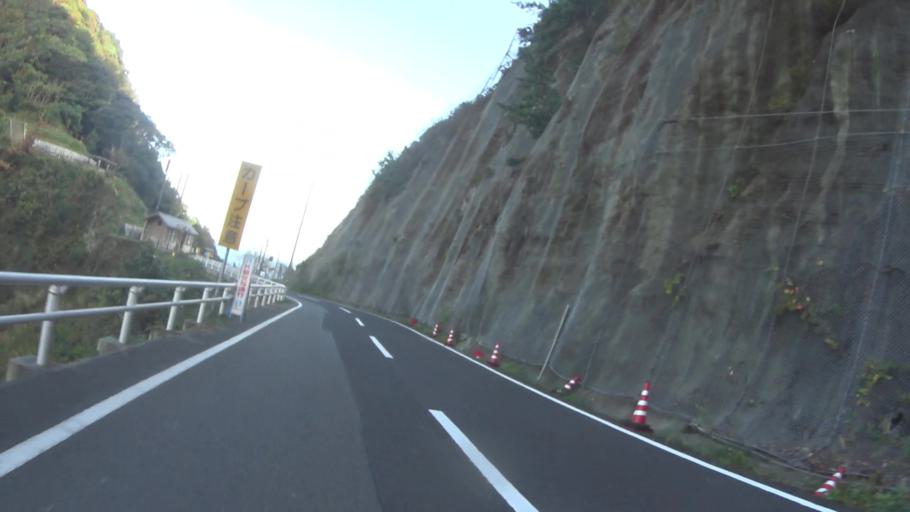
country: JP
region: Kyoto
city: Miyazu
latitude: 35.7560
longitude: 135.2501
